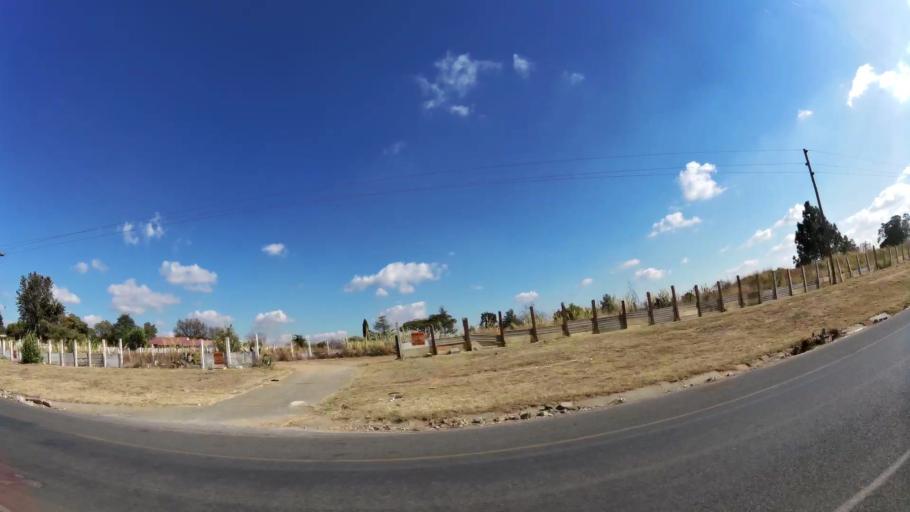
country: ZA
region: Gauteng
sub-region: West Rand District Municipality
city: Muldersdriseloop
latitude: -26.0479
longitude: 27.9066
